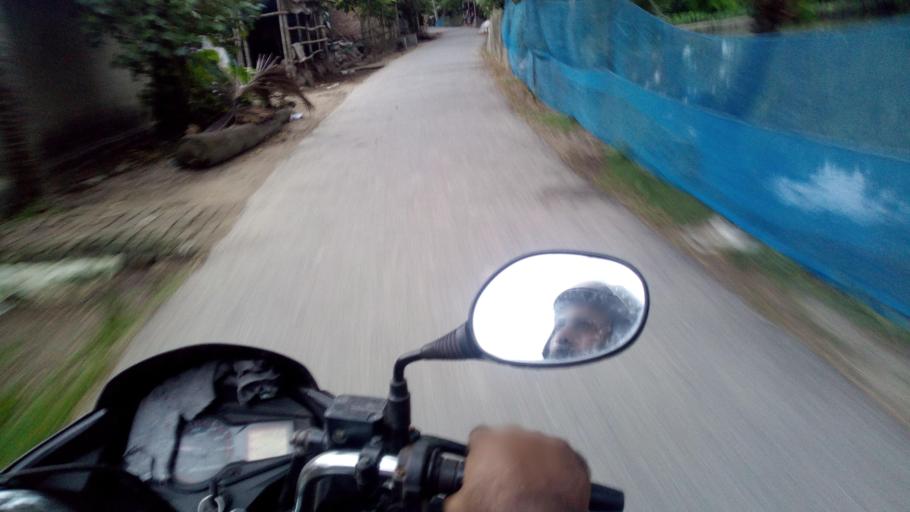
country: BD
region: Khulna
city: Phultala
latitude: 22.7695
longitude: 89.4083
